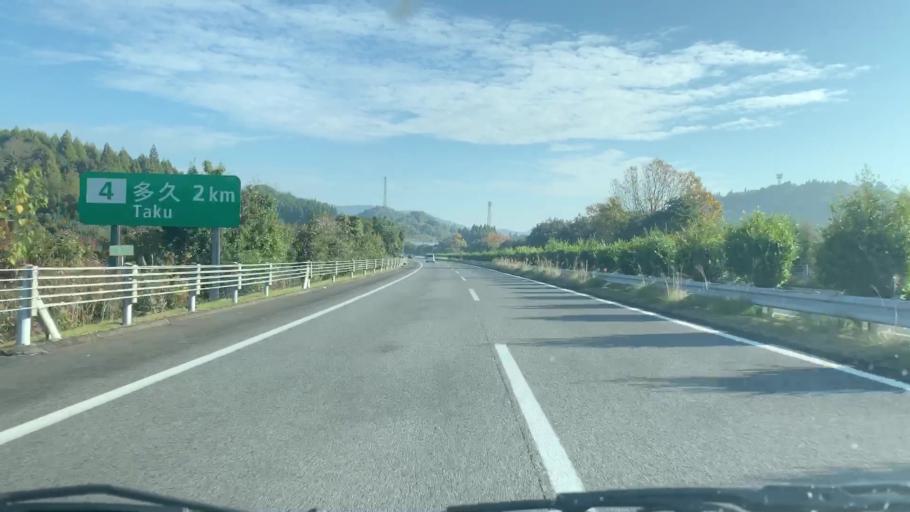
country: JP
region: Saga Prefecture
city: Takeocho-takeo
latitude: 33.2745
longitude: 130.1118
